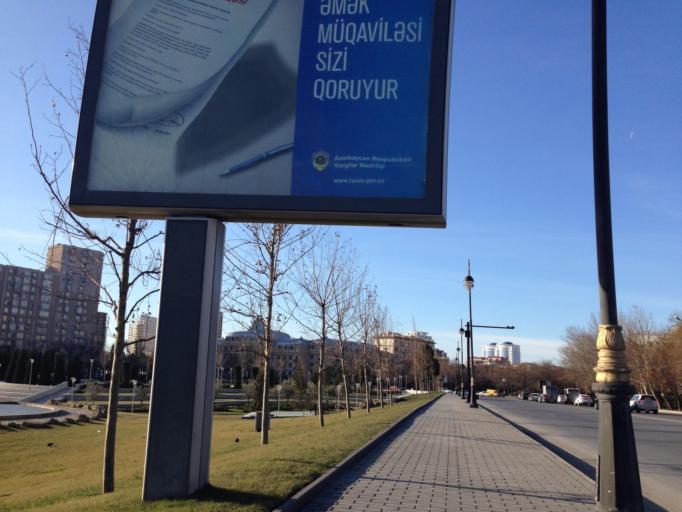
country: AZ
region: Baki
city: Baku
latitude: 40.3940
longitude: 49.8470
